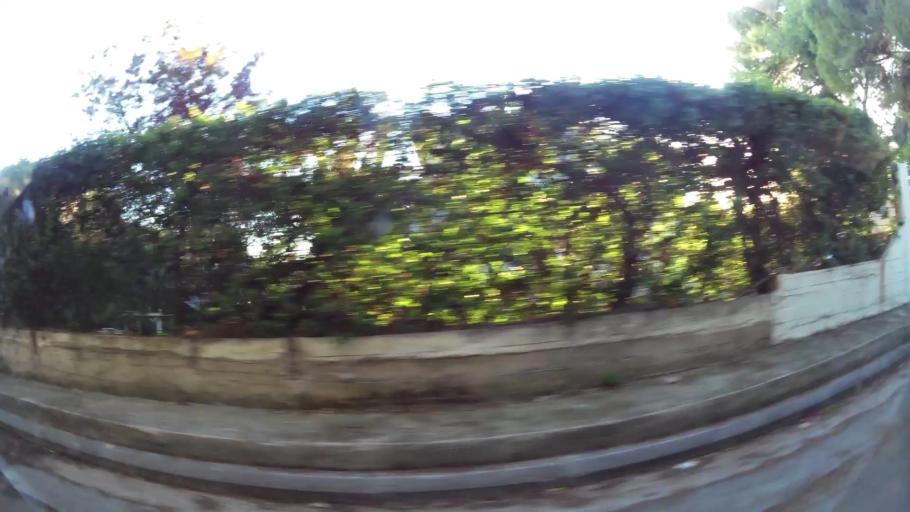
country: GR
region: Attica
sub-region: Nomarchia Anatolikis Attikis
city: Rafina
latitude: 38.0096
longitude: 24.0154
